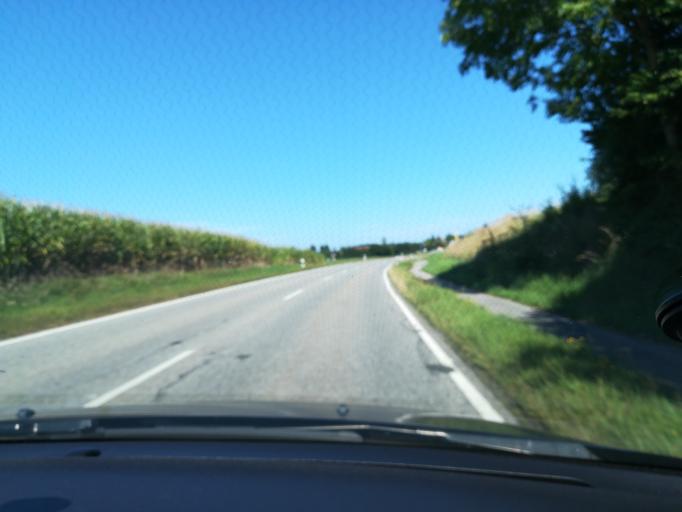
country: DE
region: Bavaria
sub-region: Upper Bavaria
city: Eggstatt
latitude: 47.9110
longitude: 12.3805
